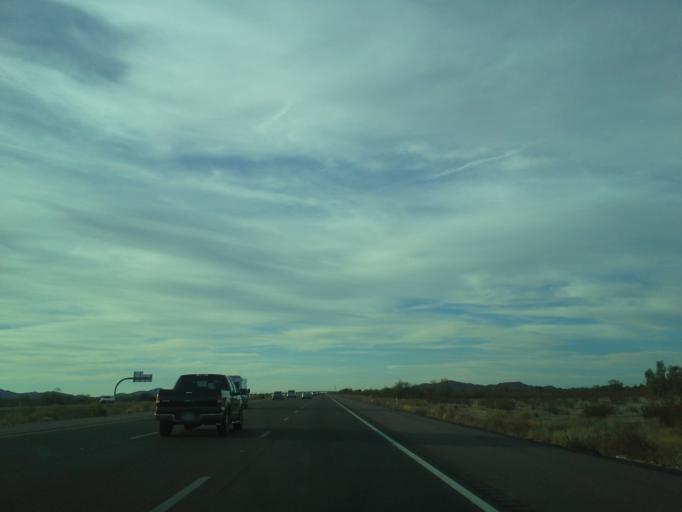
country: US
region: Arizona
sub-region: Pinal County
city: Casa Grande
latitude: 32.9530
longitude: -111.7124
